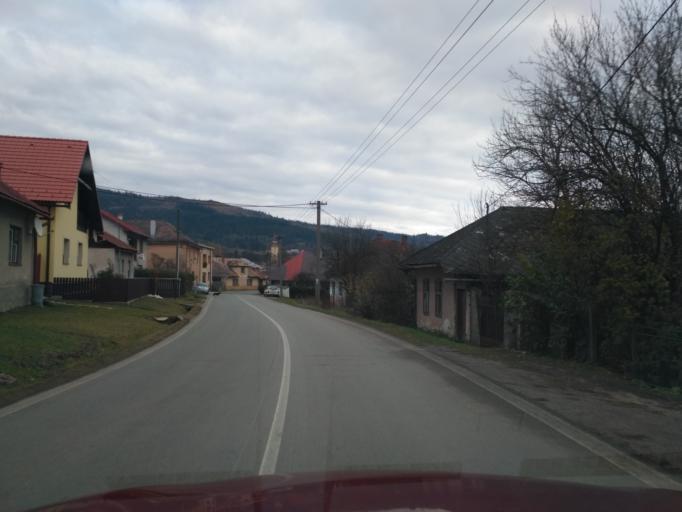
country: SK
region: Kosicky
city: Spisska Nova Ves
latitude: 48.8128
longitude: 20.7038
